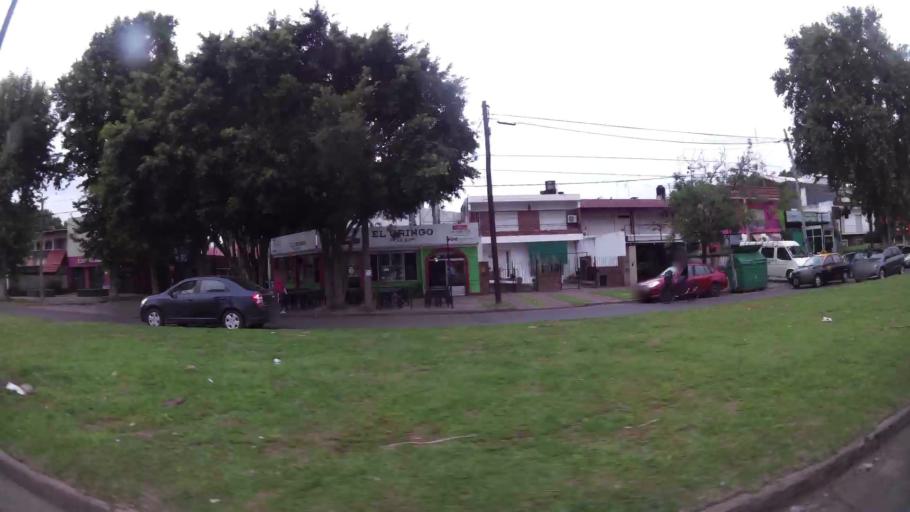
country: AR
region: Santa Fe
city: Granadero Baigorria
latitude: -32.8935
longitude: -60.6926
